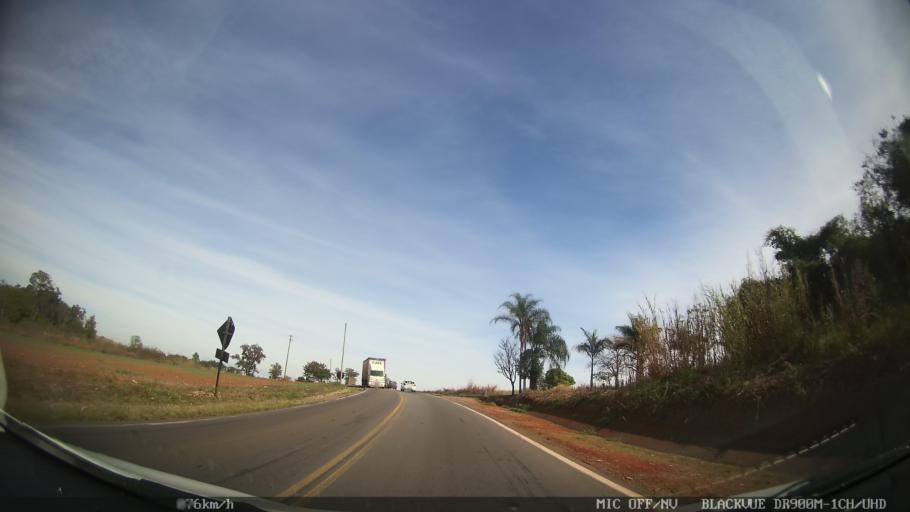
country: BR
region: Sao Paulo
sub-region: Rio Das Pedras
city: Rio das Pedras
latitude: -22.7888
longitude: -47.6348
